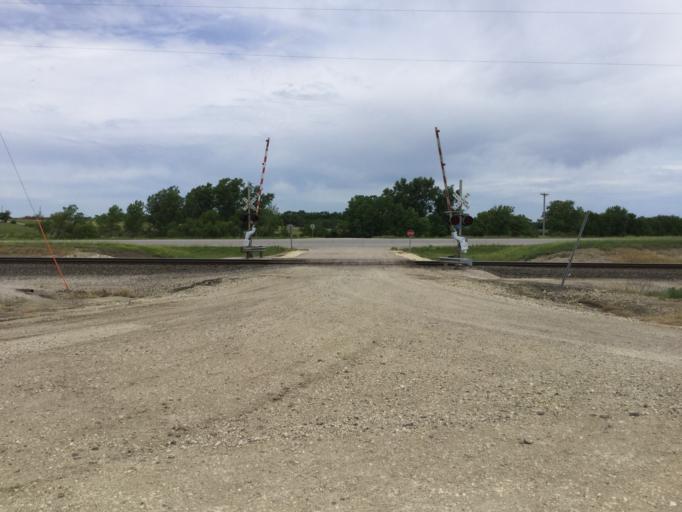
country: US
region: Kansas
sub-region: Marion County
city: Peabody
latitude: 38.1445
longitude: -97.2263
